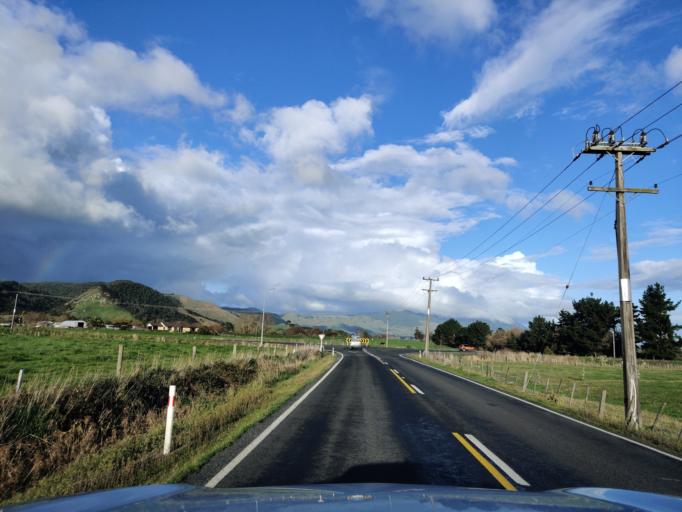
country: NZ
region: Waikato
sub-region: Hauraki District
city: Paeroa
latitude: -37.4421
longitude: 175.6312
